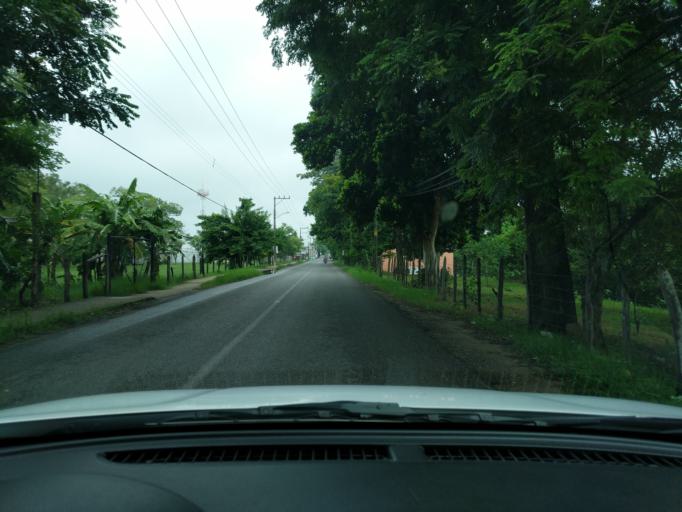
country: MX
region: Tabasco
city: Villahermosa
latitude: 17.9527
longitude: -92.9649
